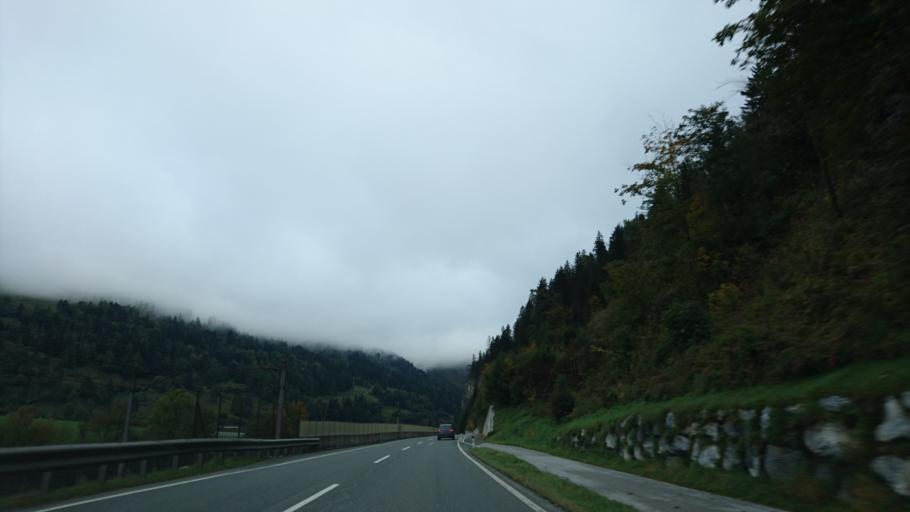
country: AT
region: Salzburg
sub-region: Politischer Bezirk Sankt Johann im Pongau
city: Dorfgastein
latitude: 47.2599
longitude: 13.0884
